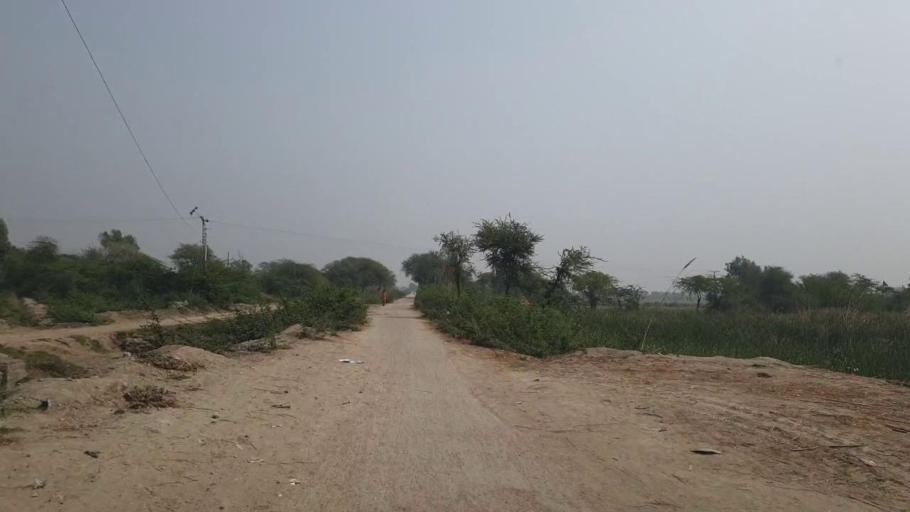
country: PK
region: Sindh
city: Kario
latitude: 24.6528
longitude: 68.6043
